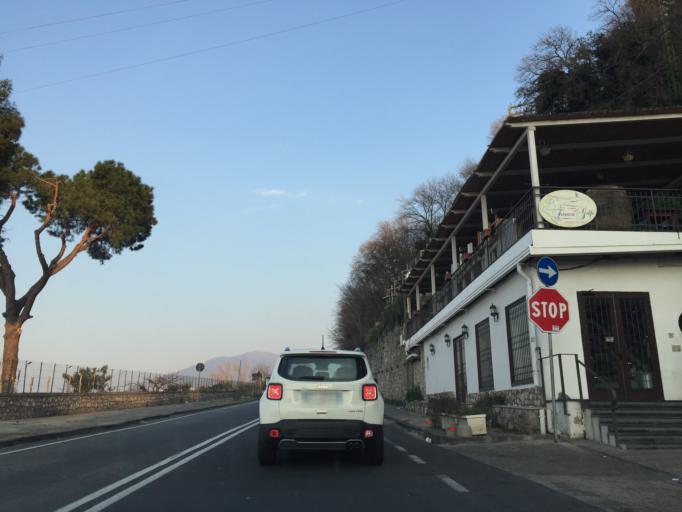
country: IT
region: Campania
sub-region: Provincia di Napoli
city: Castellammare di Stabia
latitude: 40.6888
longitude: 14.4675
